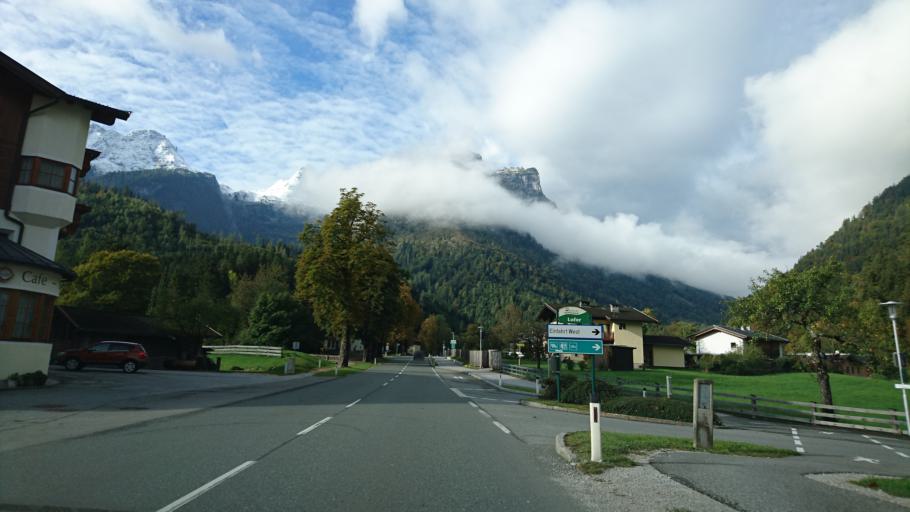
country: AT
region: Salzburg
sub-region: Politischer Bezirk Zell am See
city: Lofer
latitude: 47.5821
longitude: 12.6884
